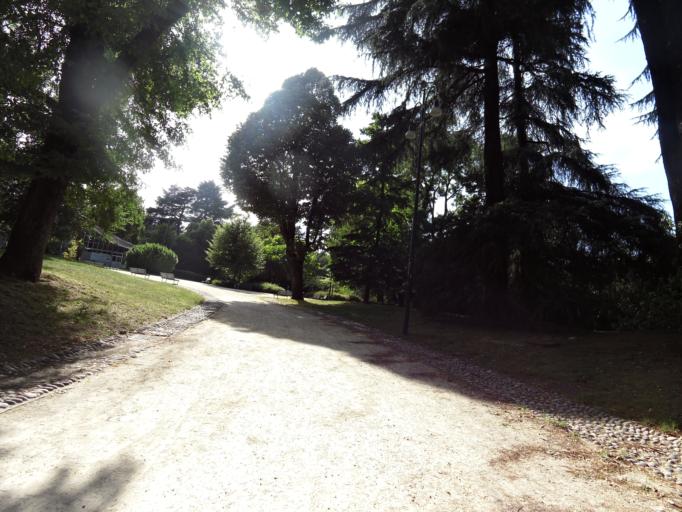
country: IT
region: Lombardy
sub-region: Citta metropolitana di Milano
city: Milano
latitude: 45.4747
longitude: 9.1760
